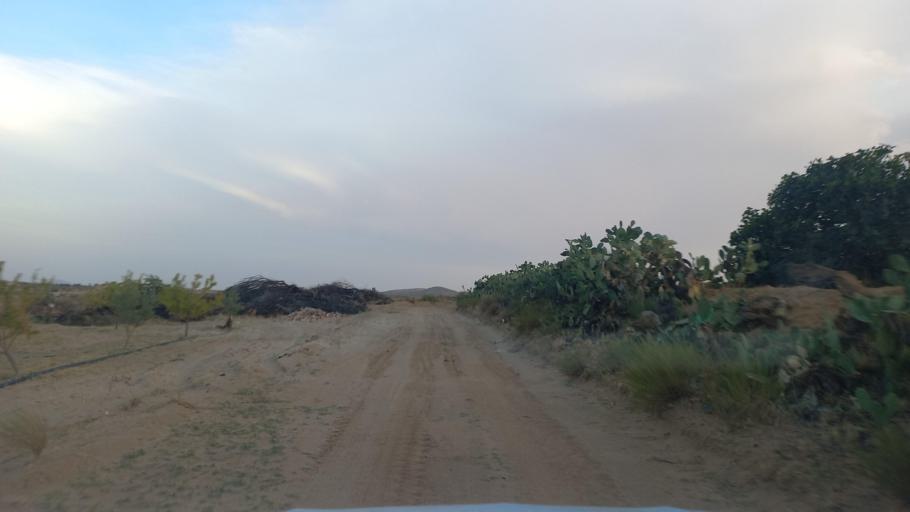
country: TN
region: Al Qasrayn
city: Kasserine
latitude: 35.1927
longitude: 9.0492
